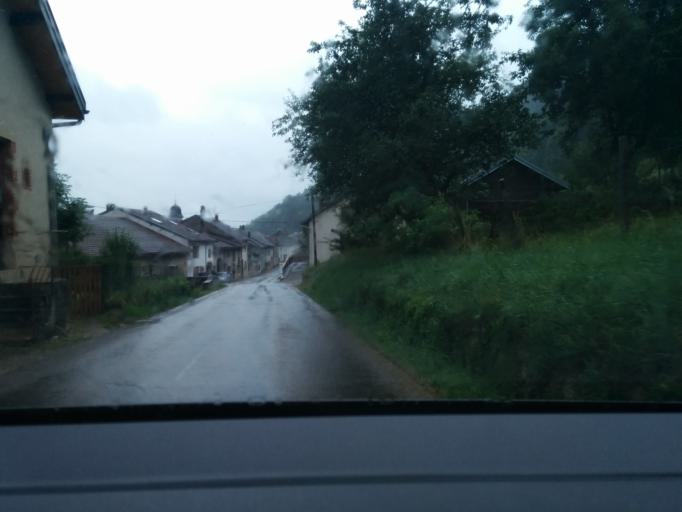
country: FR
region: Franche-Comte
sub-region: Departement du Jura
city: Valfin-les-Saint-Claude
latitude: 46.4544
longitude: 5.8281
